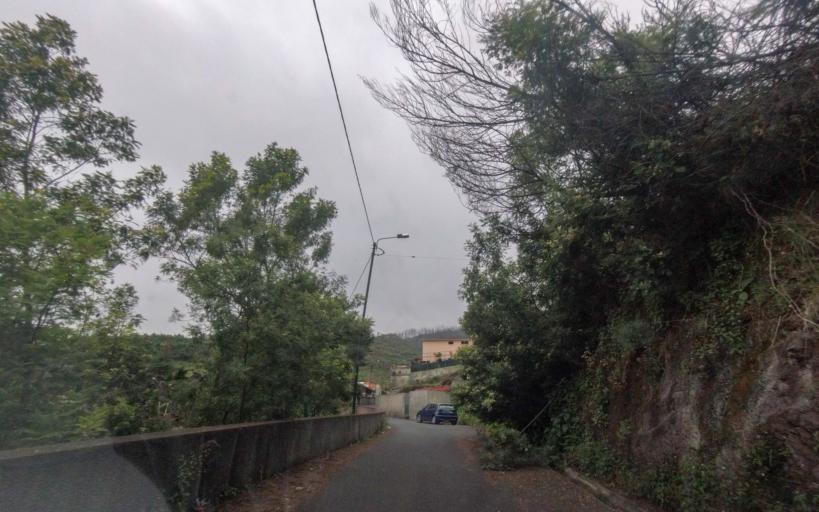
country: PT
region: Madeira
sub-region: Funchal
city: Nossa Senhora do Monte
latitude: 32.6758
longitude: -16.9127
